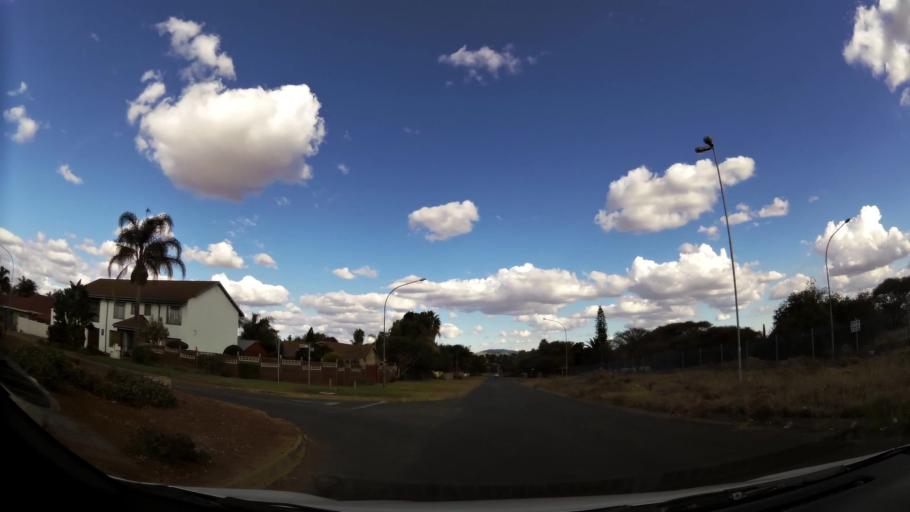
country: ZA
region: Limpopo
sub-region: Capricorn District Municipality
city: Polokwane
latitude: -23.9032
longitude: 29.4915
